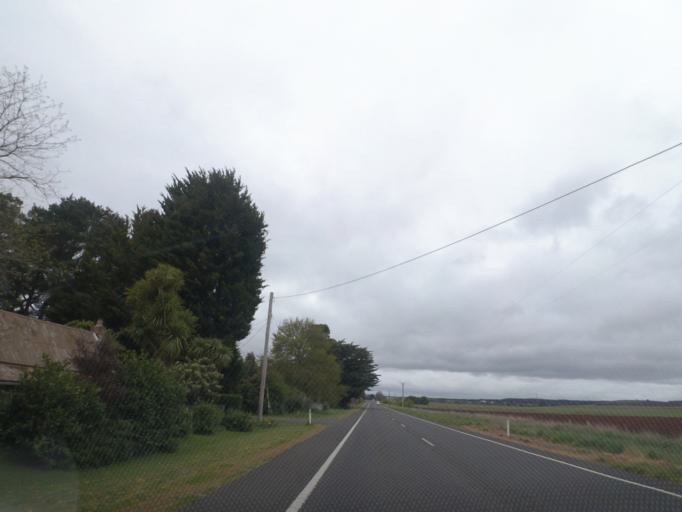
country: AU
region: Victoria
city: Brown Hill
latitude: -37.3813
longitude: 144.0138
